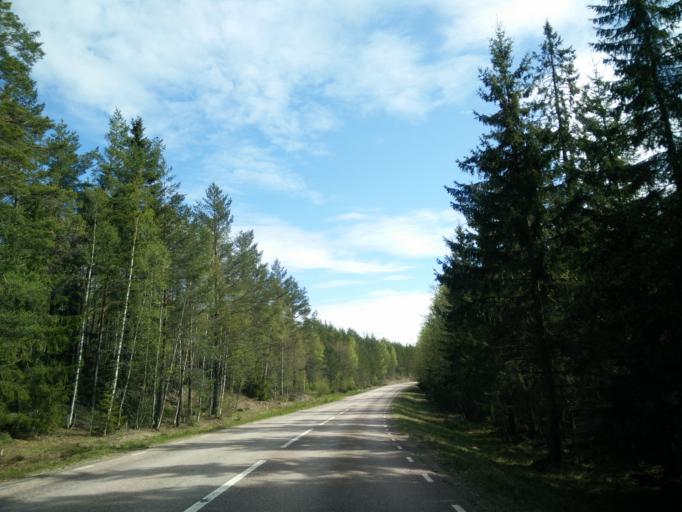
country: SE
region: Gaevleborg
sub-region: Hudiksvalls Kommun
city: Hudiksvall
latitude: 61.8543
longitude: 17.2865
